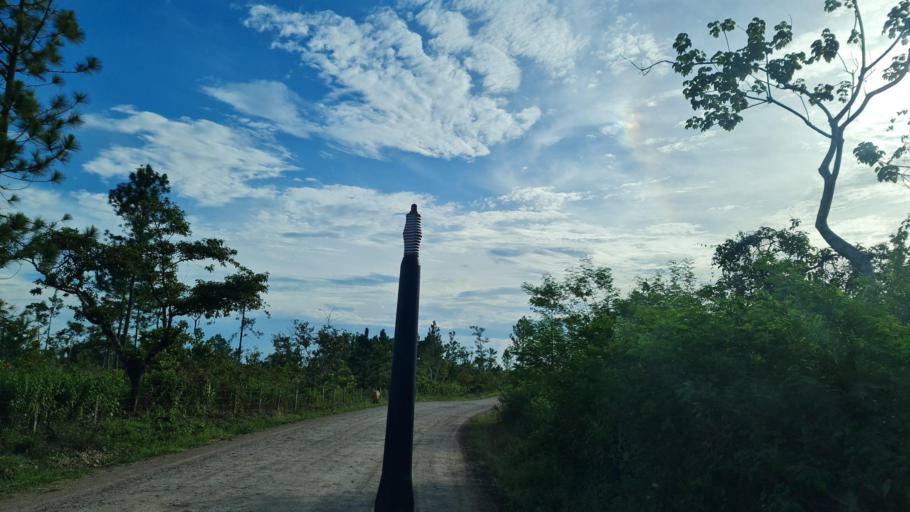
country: NI
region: Atlantico Sur
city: La Cruz de Rio Grande
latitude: 13.5562
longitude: -84.2907
